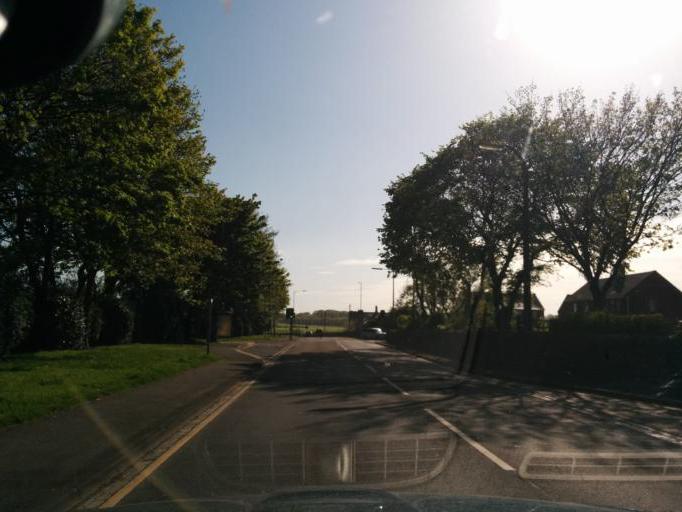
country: GB
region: England
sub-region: Northumberland
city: Newbiggin-by-the-Sea
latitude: 55.1784
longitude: -1.5212
